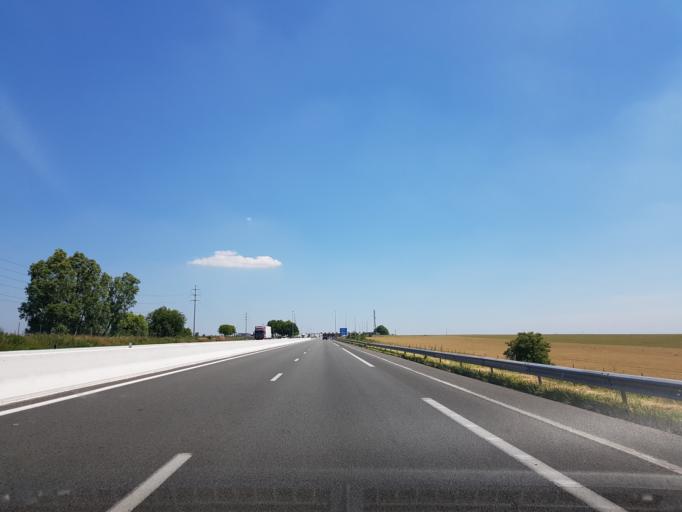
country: FR
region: Nord-Pas-de-Calais
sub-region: Departement du Nord
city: Escaudoeuvres
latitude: 50.2265
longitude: 3.2641
